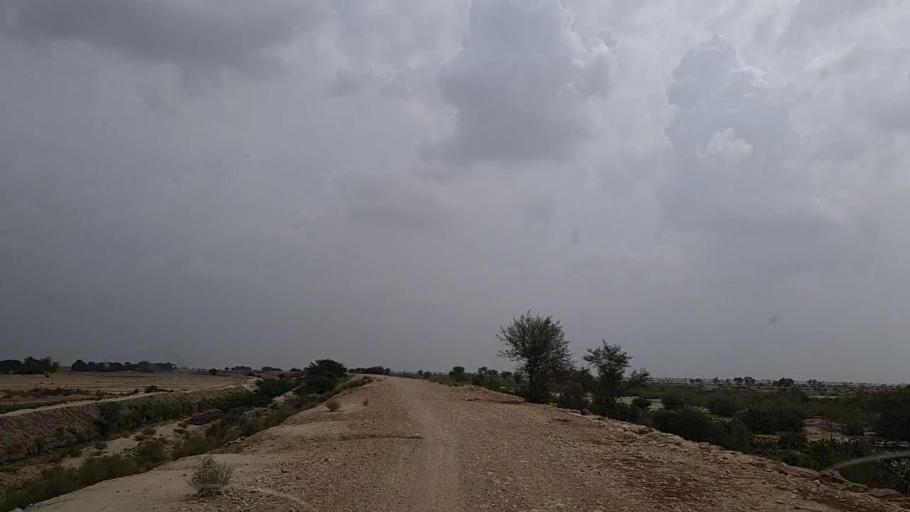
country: PK
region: Sindh
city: Johi
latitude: 26.7287
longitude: 67.5782
